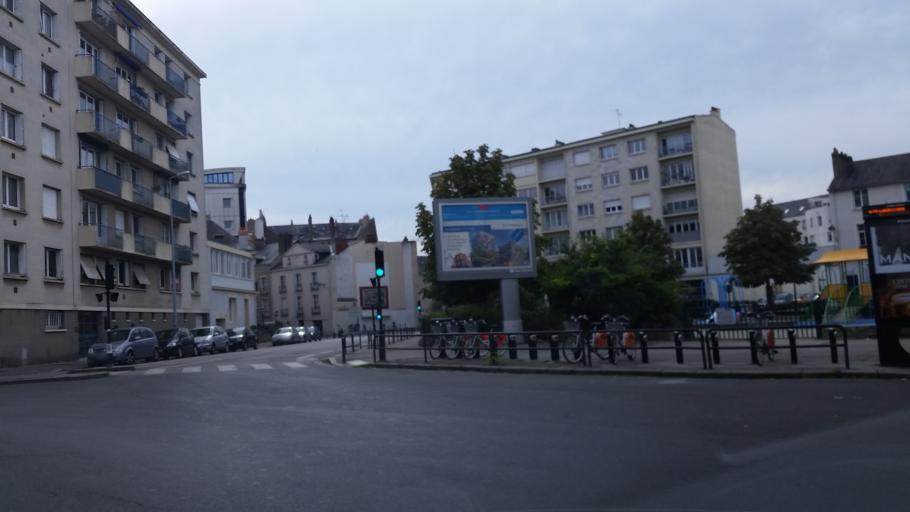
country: FR
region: Pays de la Loire
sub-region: Departement de la Loire-Atlantique
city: Nantes
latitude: 47.2096
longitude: -1.5706
